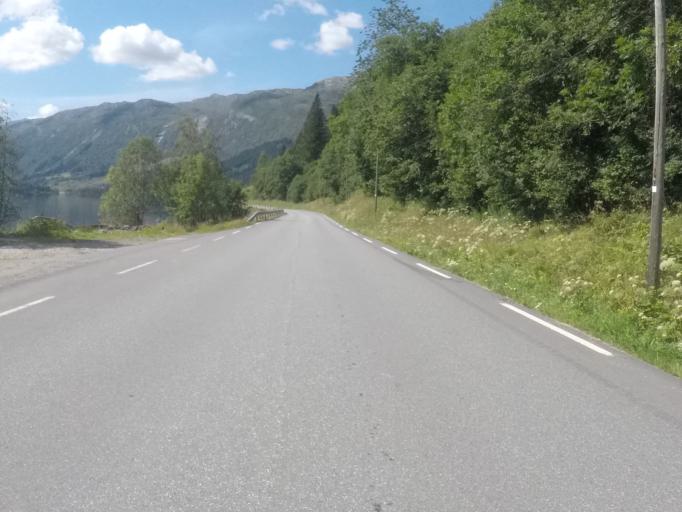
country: NO
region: Sogn og Fjordane
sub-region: Hoyanger
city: Hoyanger
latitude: 61.3588
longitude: 6.1726
